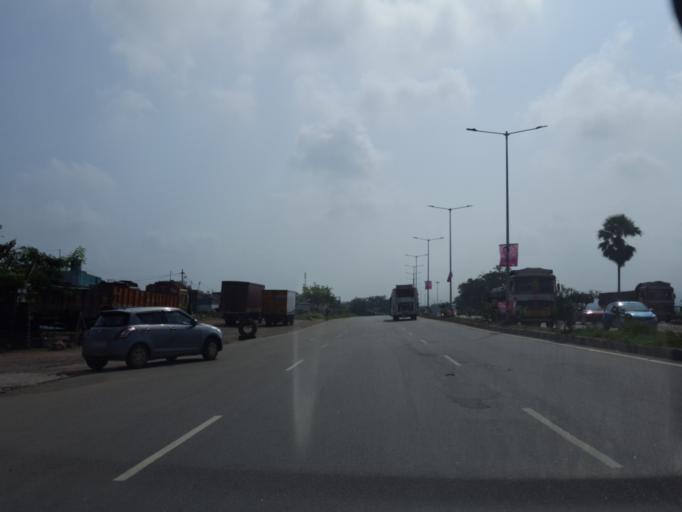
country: IN
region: Telangana
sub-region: Rangareddi
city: Lal Bahadur Nagar
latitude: 17.3159
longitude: 78.6709
